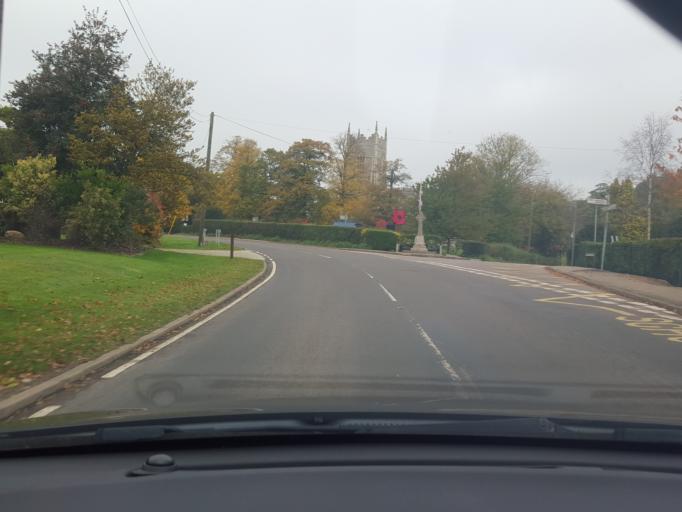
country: GB
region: England
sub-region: Essex
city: Alresford
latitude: 51.8949
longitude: 1.0270
